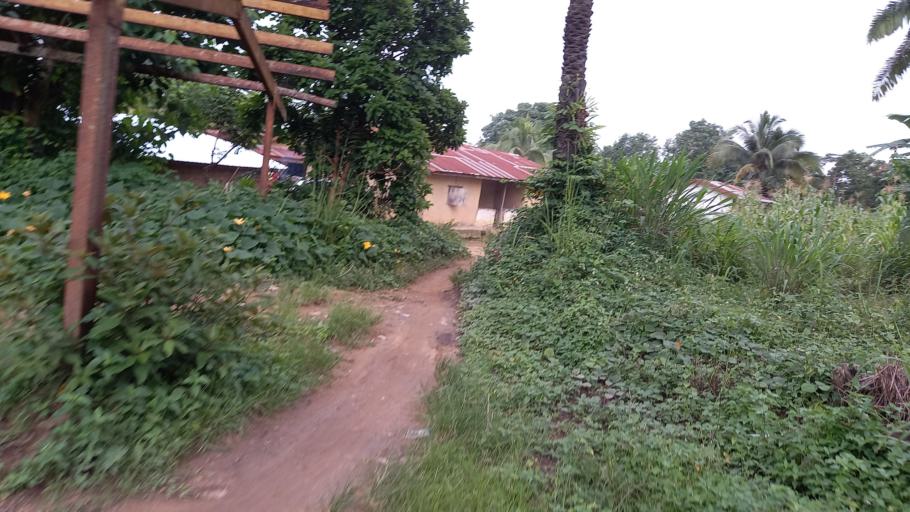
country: SL
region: Eastern Province
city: Kailahun
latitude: 8.2854
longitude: -10.5756
